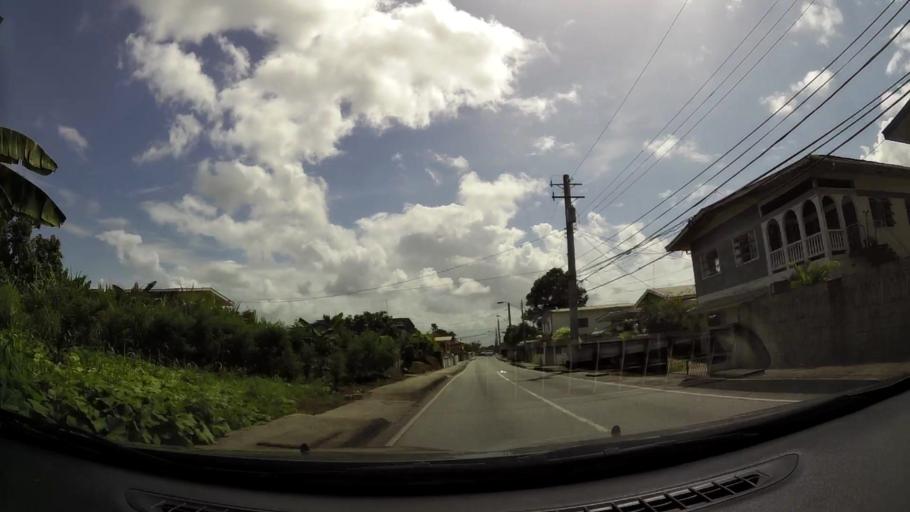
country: TT
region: Borough of Arima
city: Arima
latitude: 10.6357
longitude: -61.2763
